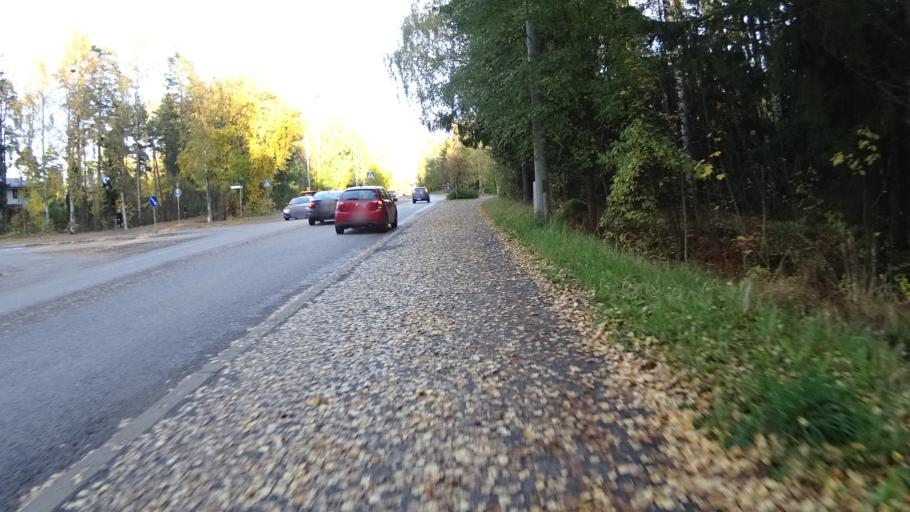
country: FI
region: Uusimaa
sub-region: Helsinki
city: Helsinki
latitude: 60.2307
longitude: 24.9510
